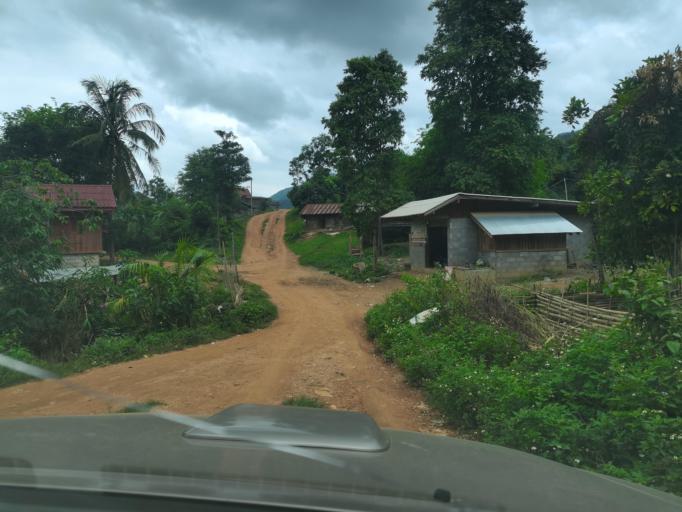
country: TH
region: Phayao
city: Phu Sang
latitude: 19.7466
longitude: 100.4283
